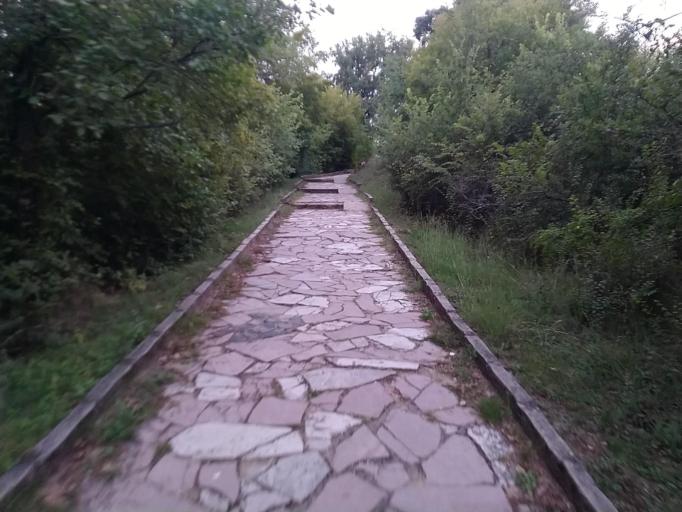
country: BG
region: Plovdiv
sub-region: Obshtina Khisarya
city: Khisarya
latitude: 42.4965
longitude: 24.7033
